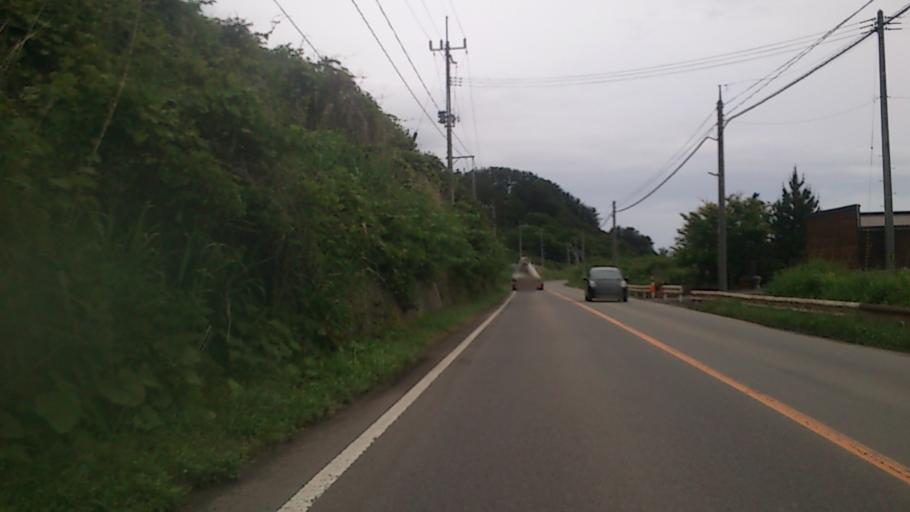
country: JP
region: Akita
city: Noshiromachi
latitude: 40.5094
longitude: 139.9507
